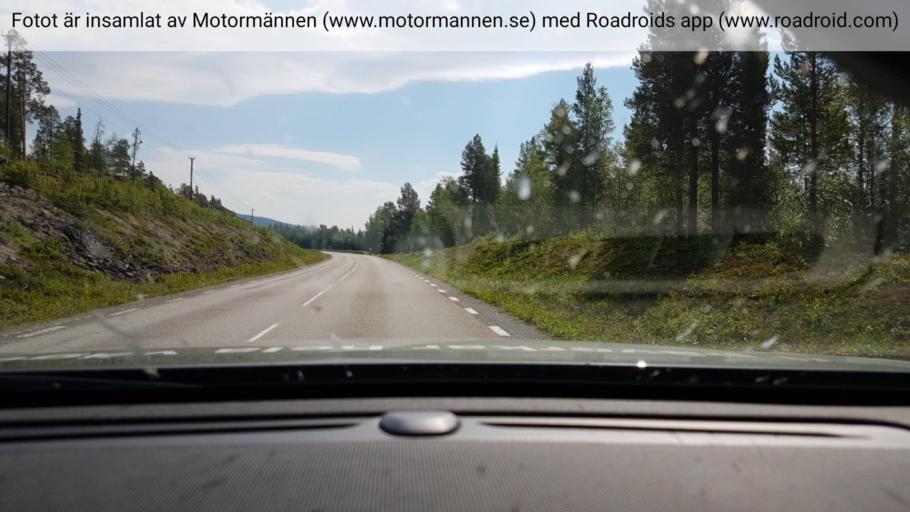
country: SE
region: Vaesterbotten
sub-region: Vilhelmina Kommun
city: Sjoberg
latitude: 65.5391
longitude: 15.5880
